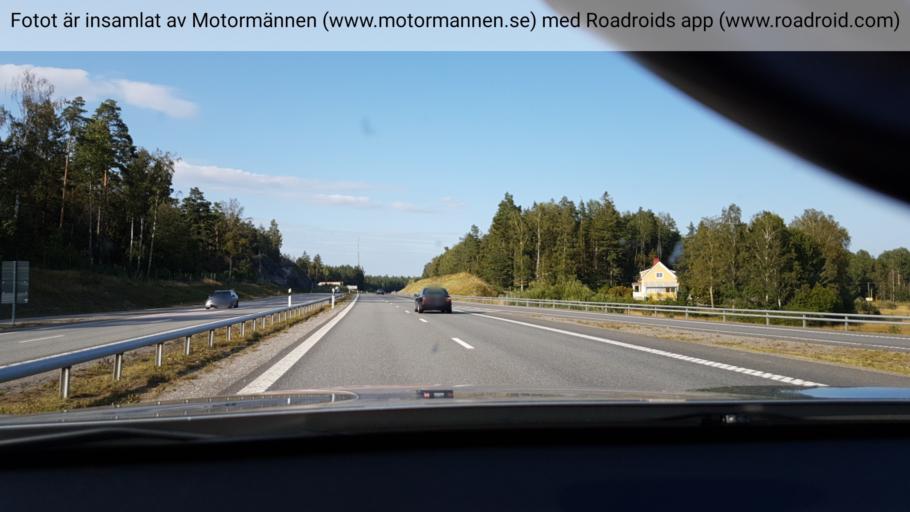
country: SE
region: Stockholm
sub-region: Haninge Kommun
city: Jordbro
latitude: 59.0697
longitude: 18.0652
